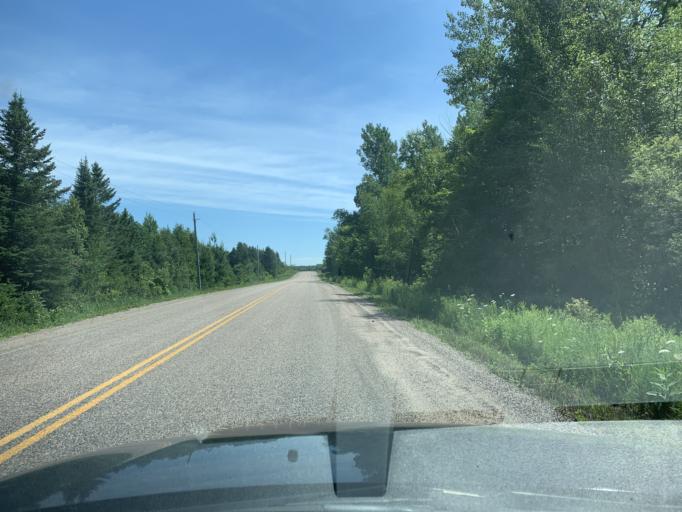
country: CA
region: Ontario
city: Pembroke
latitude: 45.4388
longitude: -77.2944
